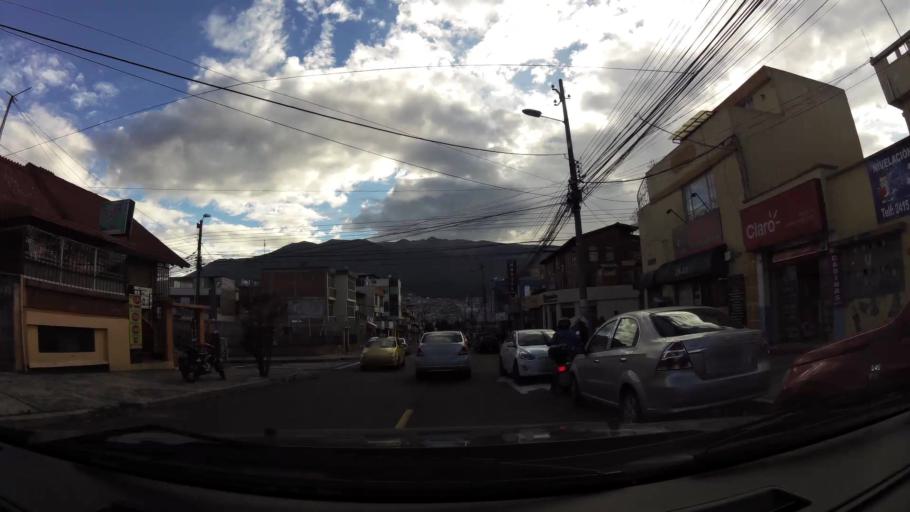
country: EC
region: Pichincha
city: Quito
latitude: -0.1409
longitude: -78.4802
